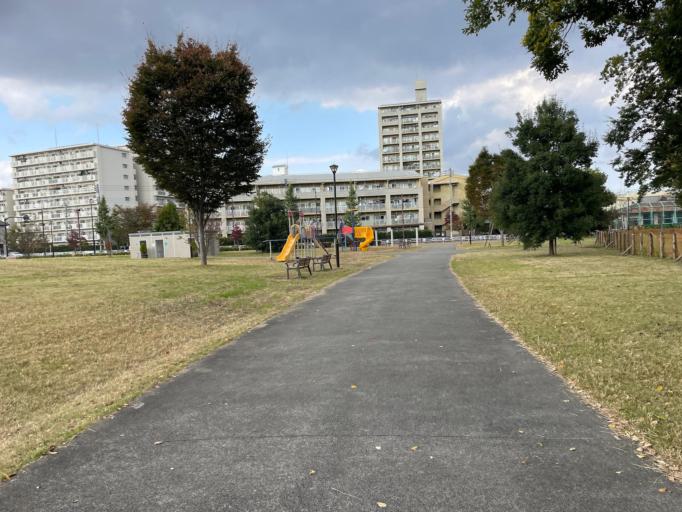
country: JP
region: Tokyo
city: Hino
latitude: 35.7184
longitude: 139.3891
